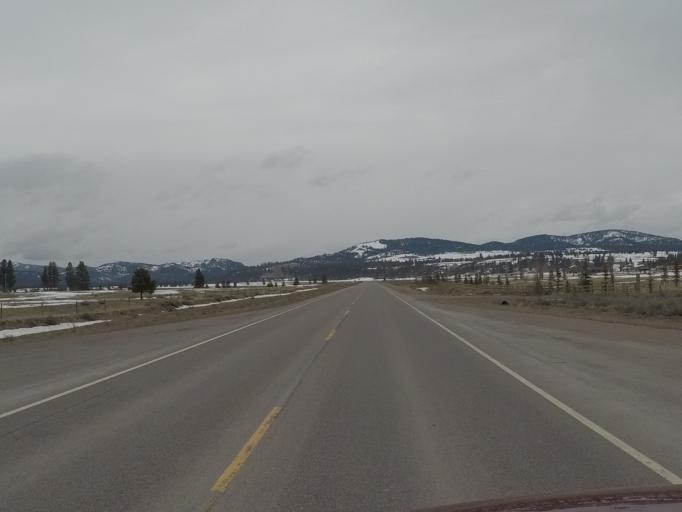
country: US
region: Montana
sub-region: Missoula County
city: Seeley Lake
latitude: 47.0093
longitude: -113.3718
